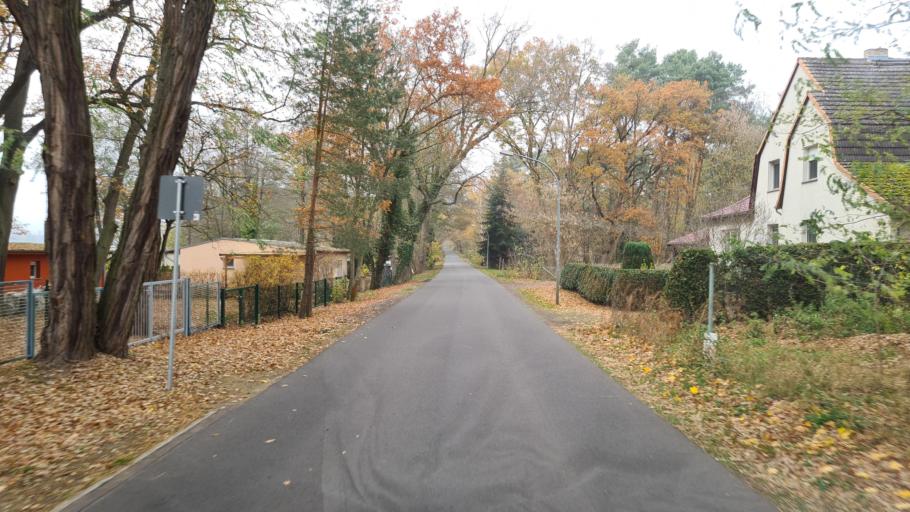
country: DE
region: Brandenburg
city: Gross Kreutz
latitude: 52.3460
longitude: 12.7259
